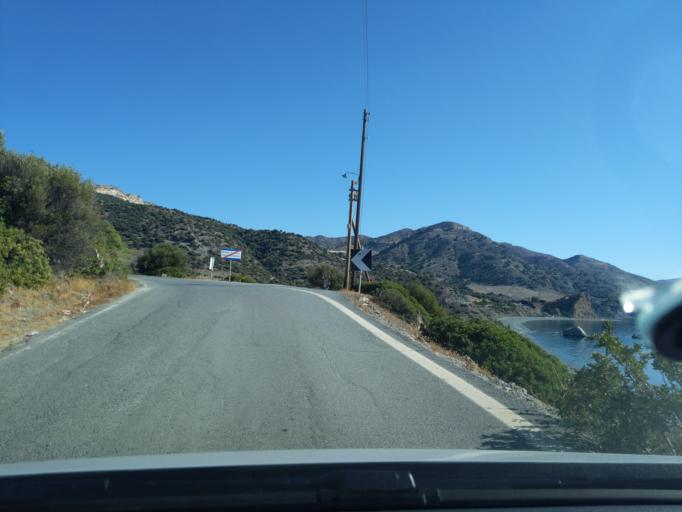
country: GR
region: Crete
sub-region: Nomos Irakleiou
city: Moires
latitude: 34.9331
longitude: 24.8039
